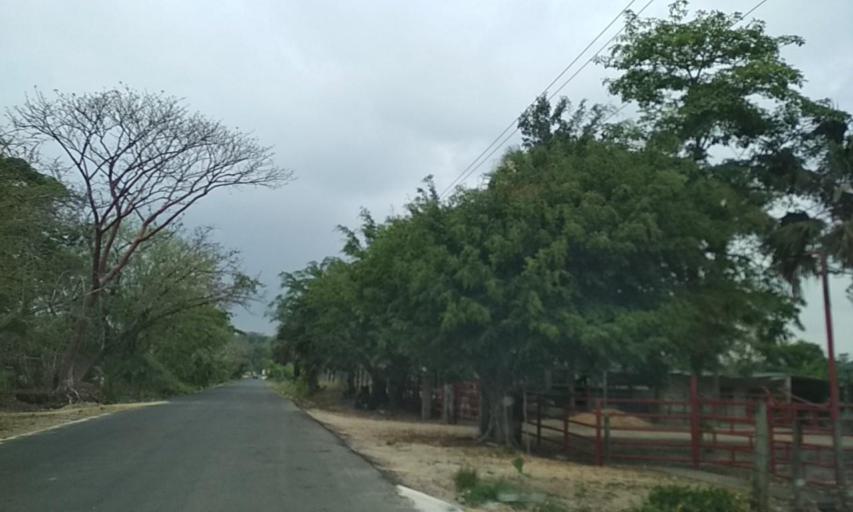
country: MX
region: Tabasco
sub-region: Huimanguillo
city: Francisco Rueda
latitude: 17.7328
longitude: -94.1040
